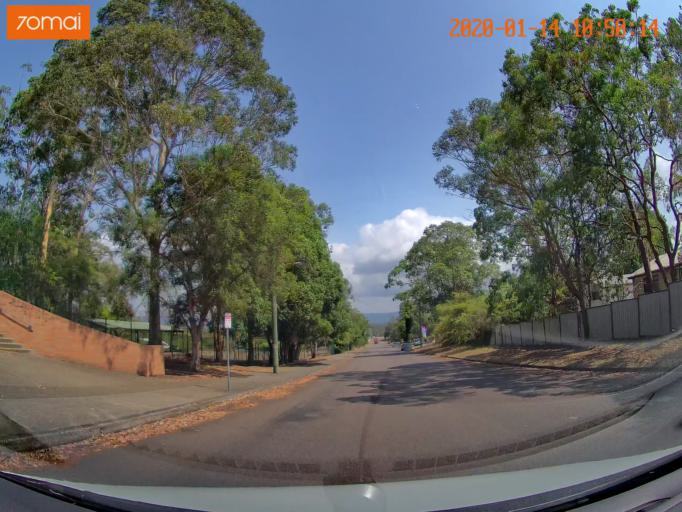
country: AU
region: New South Wales
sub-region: Lake Macquarie Shire
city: Dora Creek
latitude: -33.1045
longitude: 151.4879
